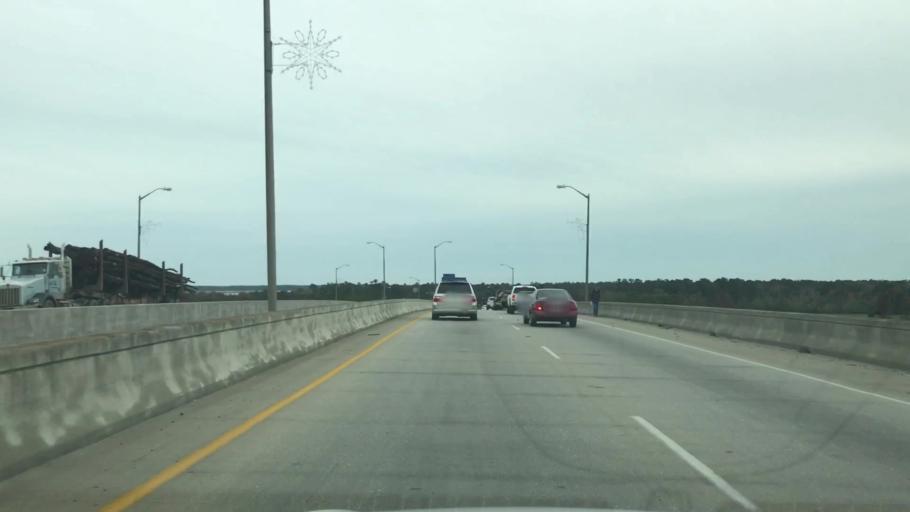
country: US
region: South Carolina
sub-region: Georgetown County
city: Georgetown
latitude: 33.3585
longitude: -79.2946
